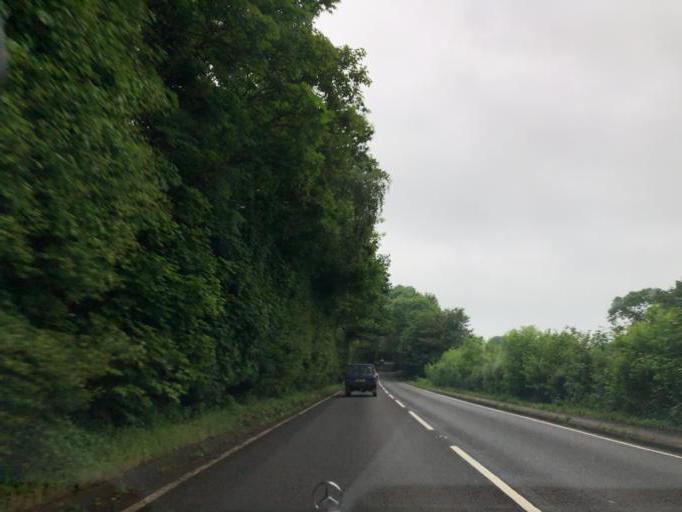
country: GB
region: England
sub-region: Warwickshire
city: Wroxall
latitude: 52.3156
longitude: -1.6665
